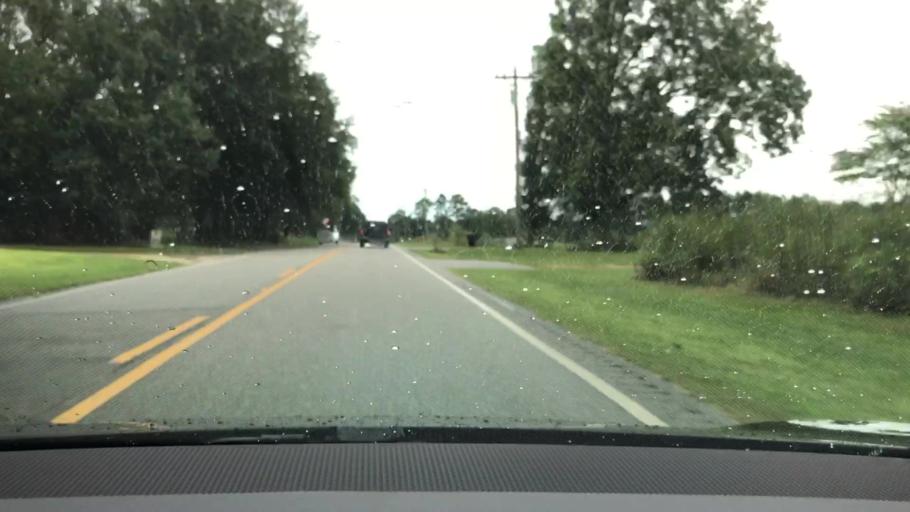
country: US
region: Alabama
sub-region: Geneva County
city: Samson
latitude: 31.0804
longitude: -86.1056
